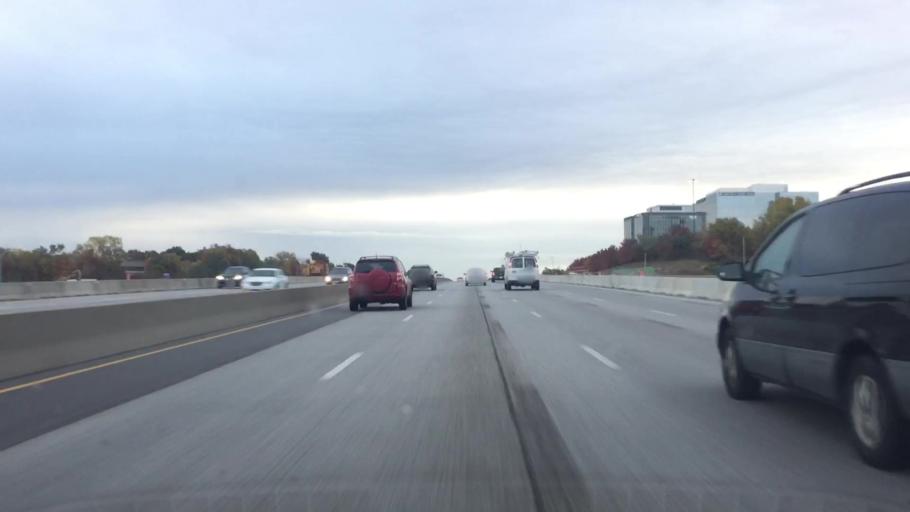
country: US
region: Kansas
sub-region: Johnson County
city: Leawood
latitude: 38.9336
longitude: -94.6150
